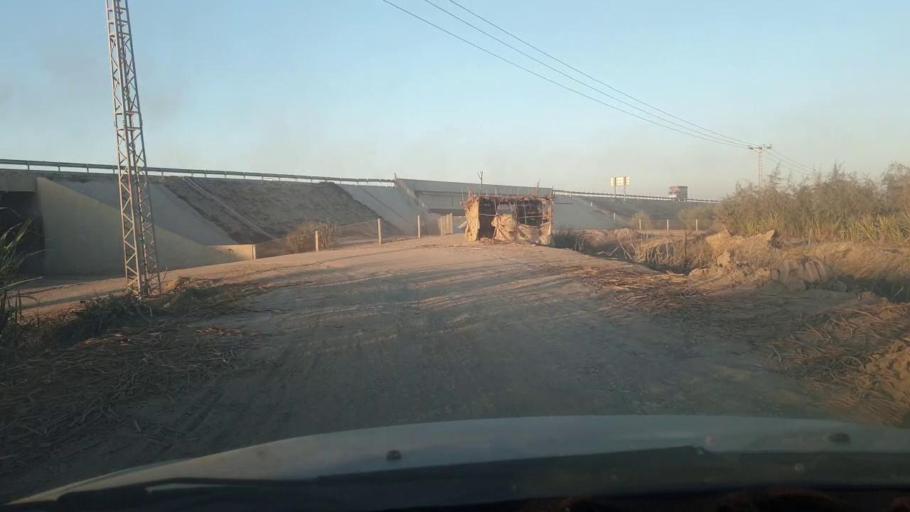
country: PK
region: Sindh
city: Ghotki
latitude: 28.0436
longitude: 69.3251
